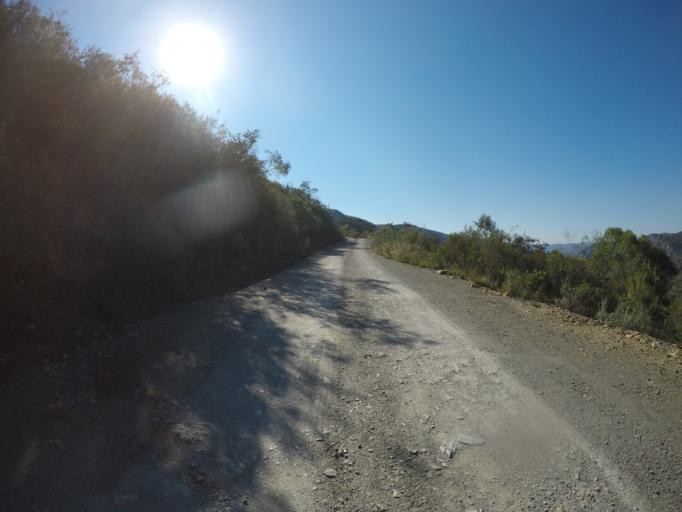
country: ZA
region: Eastern Cape
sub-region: Cacadu District Municipality
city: Kareedouw
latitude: -33.6550
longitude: 24.5072
